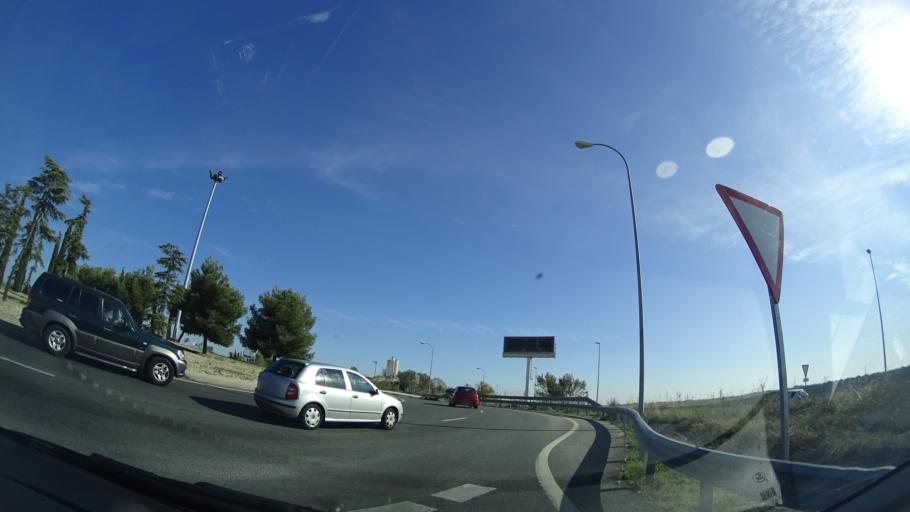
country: ES
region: Madrid
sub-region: Provincia de Madrid
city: Majadahonda
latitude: 40.4791
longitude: -3.8981
